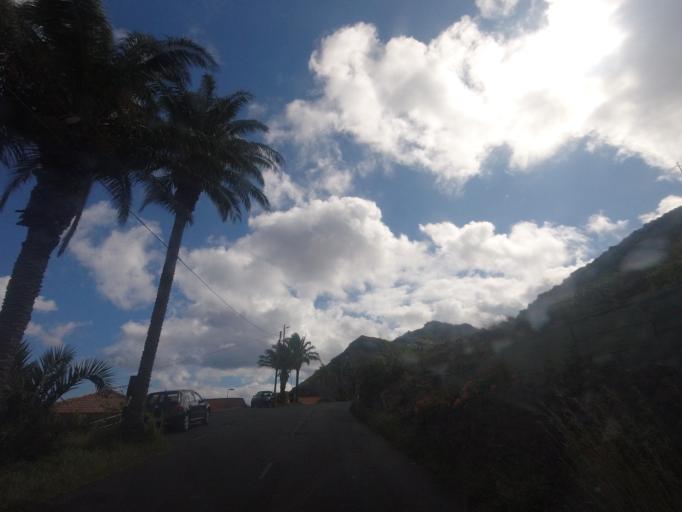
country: PT
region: Madeira
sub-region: Machico
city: Canical
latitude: 32.7399
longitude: -16.7464
